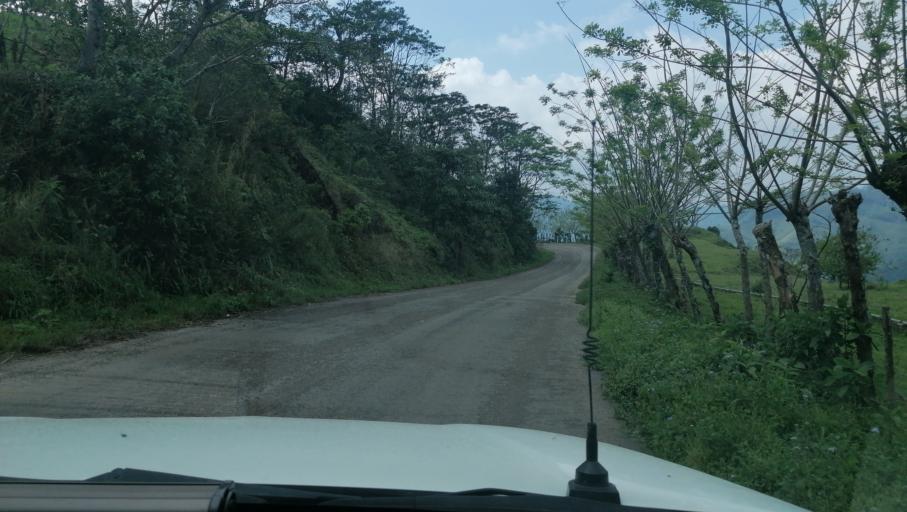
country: MX
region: Chiapas
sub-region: Francisco Leon
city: San Miguel la Sardina
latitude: 17.2383
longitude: -93.3042
